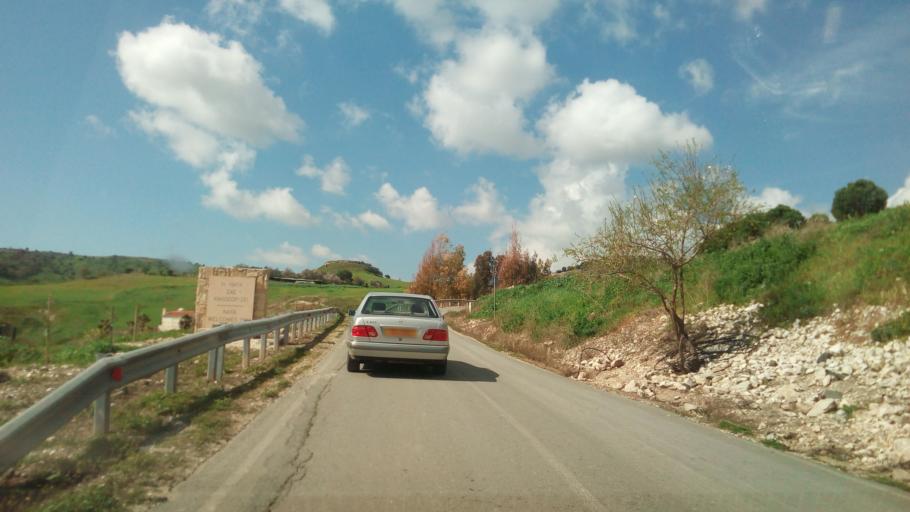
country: CY
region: Pafos
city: Mesogi
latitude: 34.7754
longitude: 32.5713
